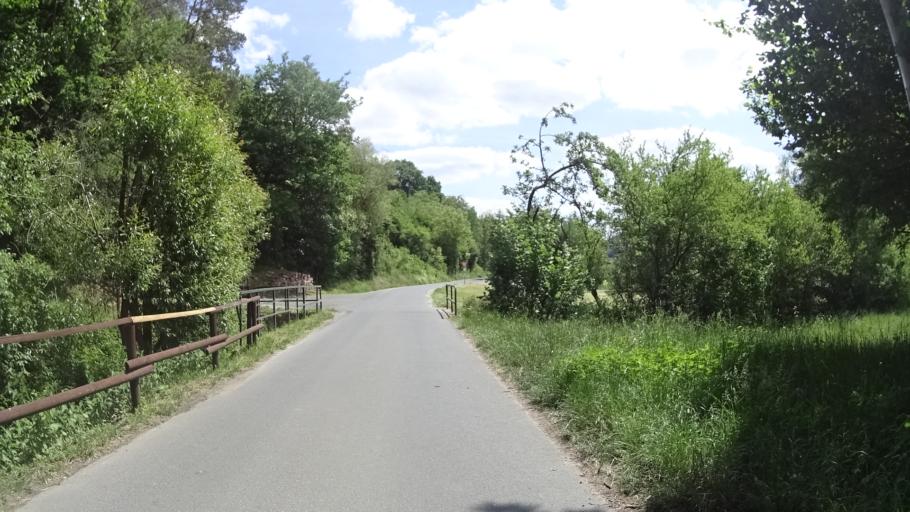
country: DE
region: Bavaria
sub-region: Regierungsbezirk Unterfranken
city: Eichenbuhl
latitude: 49.7100
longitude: 9.3212
